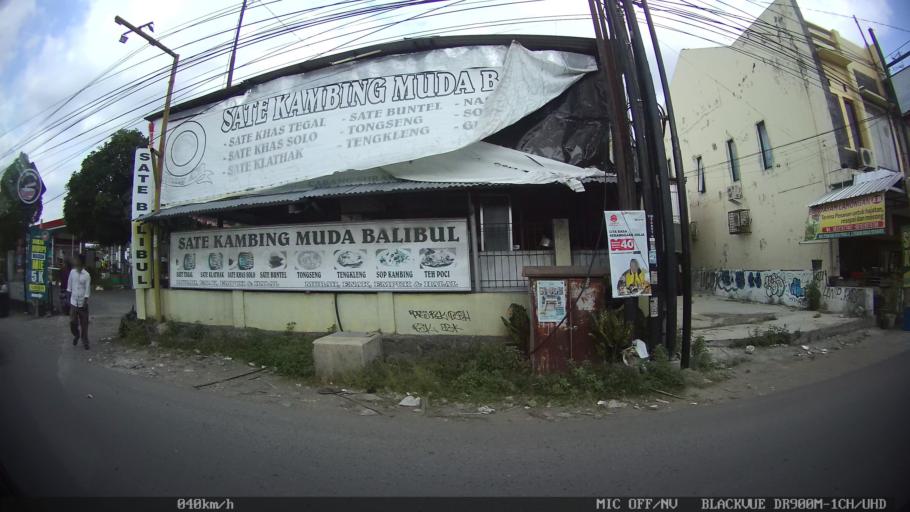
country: ID
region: Daerah Istimewa Yogyakarta
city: Yogyakarta
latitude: -7.7806
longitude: 110.3429
